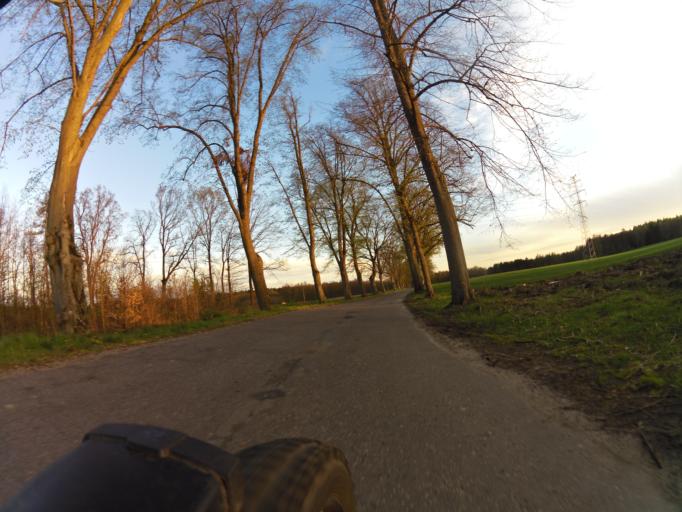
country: PL
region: West Pomeranian Voivodeship
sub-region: Powiat lobeski
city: Lobez
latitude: 53.6951
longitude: 15.6401
